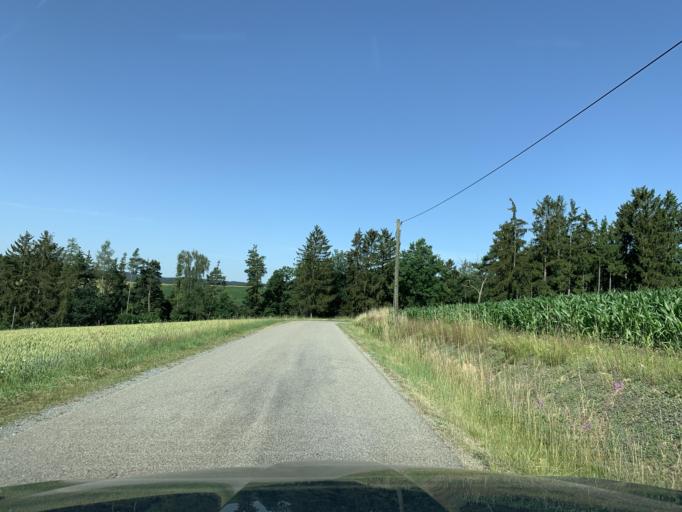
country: DE
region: Bavaria
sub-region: Upper Palatinate
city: Dieterskirchen
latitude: 49.4109
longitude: 12.4207
